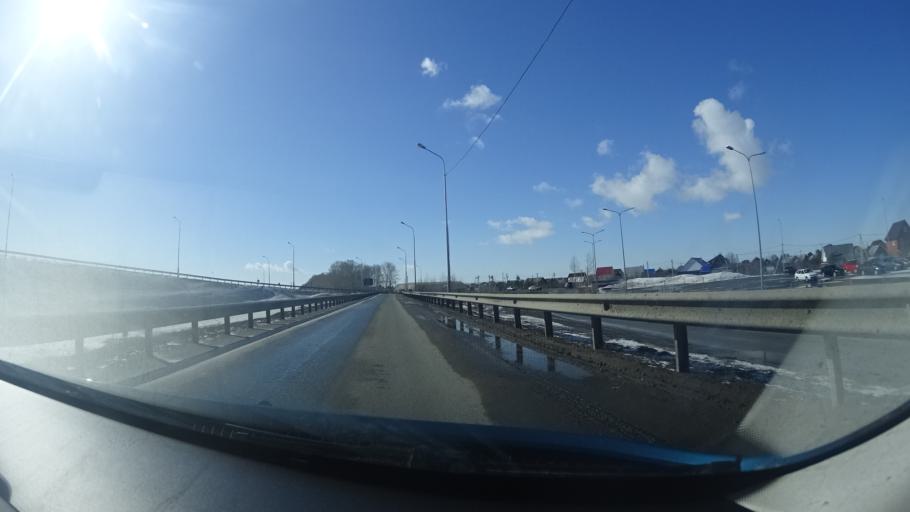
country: RU
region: Bashkortostan
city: Ufa
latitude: 54.6344
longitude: 55.9281
